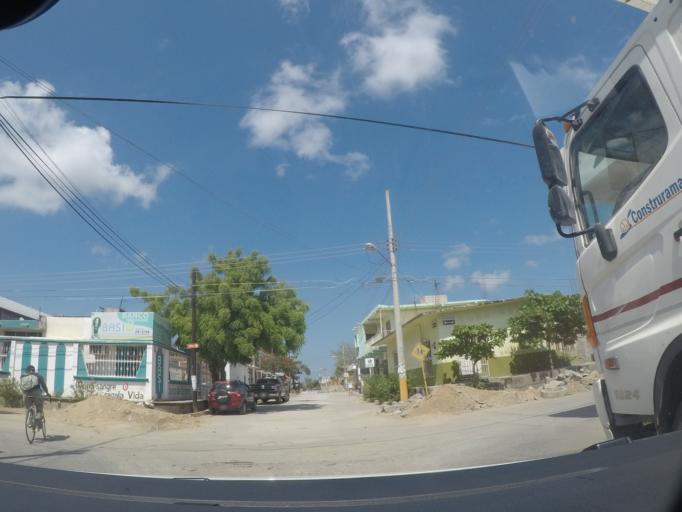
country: MX
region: Oaxaca
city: Juchitan de Zaragoza
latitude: 16.4350
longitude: -95.0160
